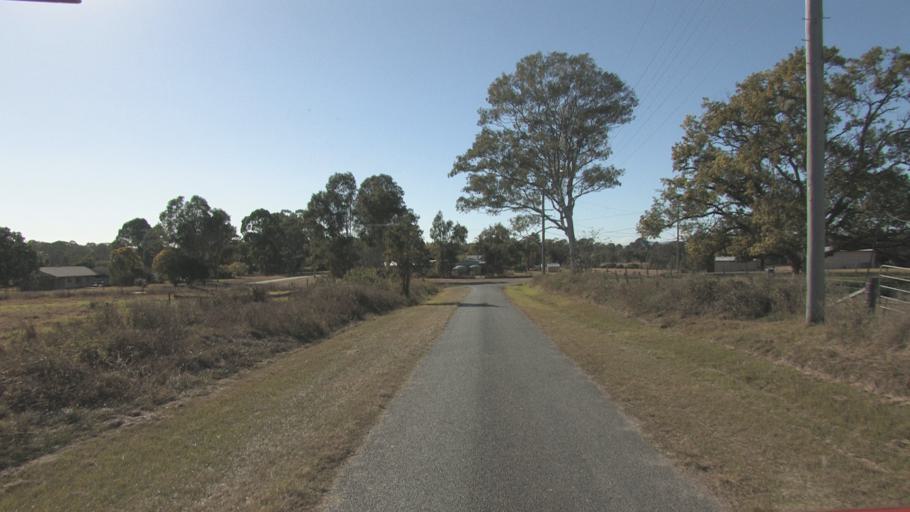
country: AU
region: Queensland
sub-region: Logan
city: North Maclean
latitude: -27.7639
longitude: 153.0466
